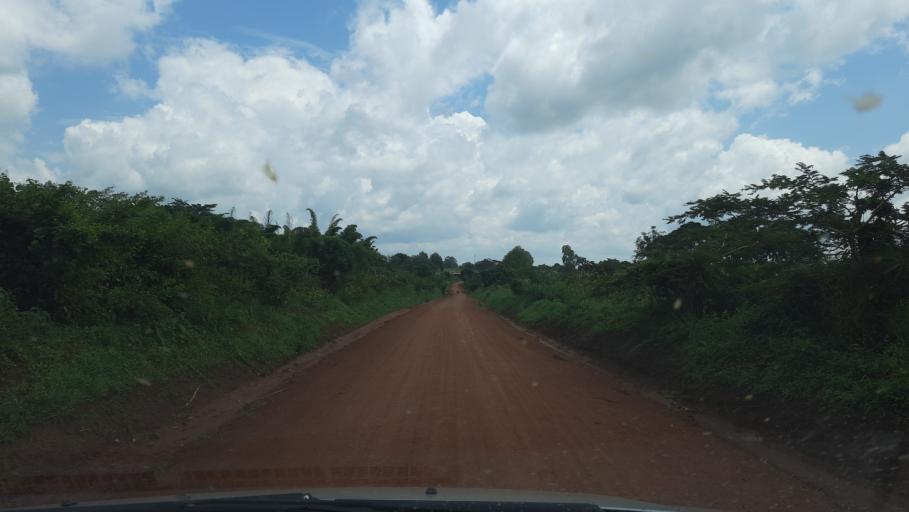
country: UG
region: Western Region
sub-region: Kiryandongo District
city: Kiryandongo
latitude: 1.8151
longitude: 31.9936
